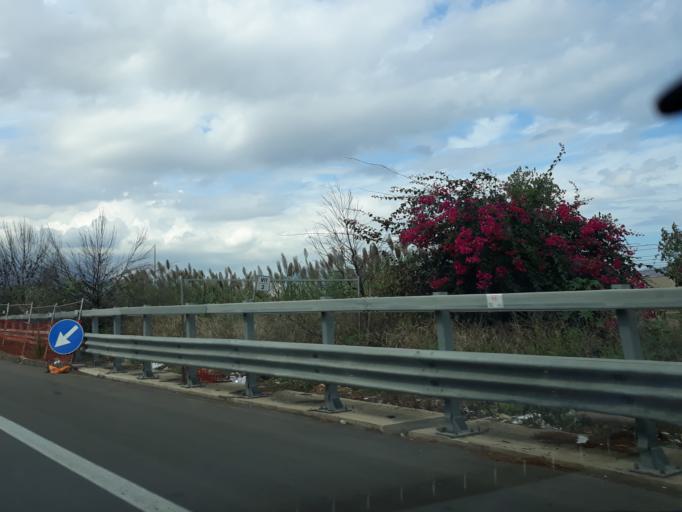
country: IT
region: Sicily
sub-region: Palermo
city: Ciaculli
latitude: 38.0860
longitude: 13.4145
